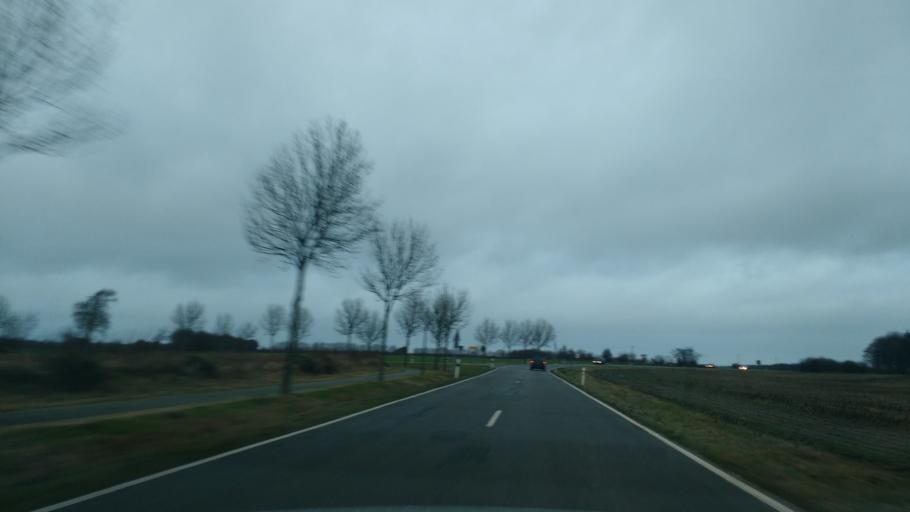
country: DE
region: Schleswig-Holstein
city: Nindorf
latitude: 54.1258
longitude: 9.7081
